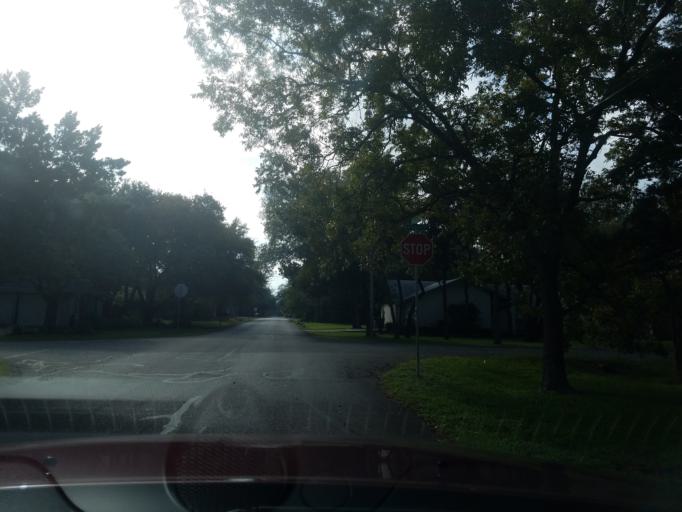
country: US
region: Texas
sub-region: Williamson County
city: Jollyville
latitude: 30.4566
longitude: -97.7854
